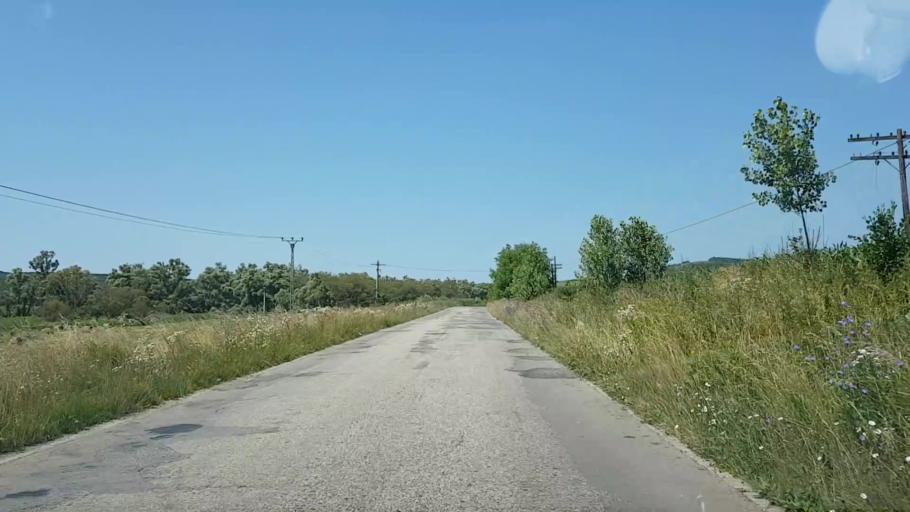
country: RO
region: Sibiu
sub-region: Comuna Iacobeni
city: Iacobeni
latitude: 46.0439
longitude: 24.7550
